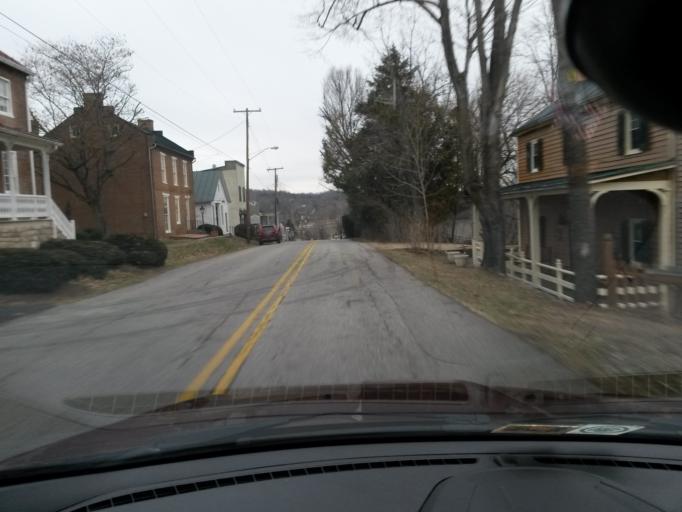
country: US
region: Virginia
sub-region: Rockbridge County
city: East Lexington
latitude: 37.9277
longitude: -79.3197
